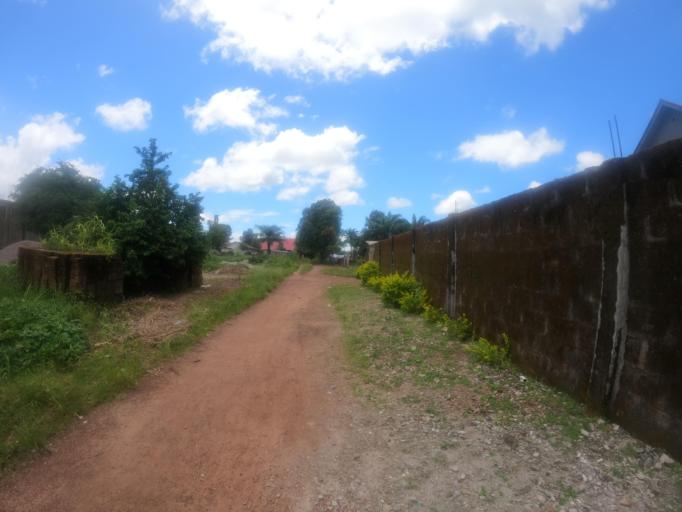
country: SL
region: Northern Province
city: Makeni
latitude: 8.8773
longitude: -12.0939
